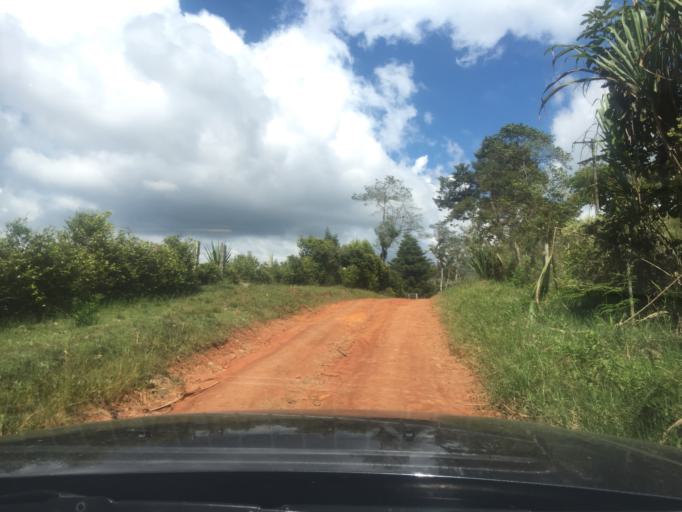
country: CO
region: Valle del Cauca
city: Yumbo
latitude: 3.6594
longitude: -76.5492
